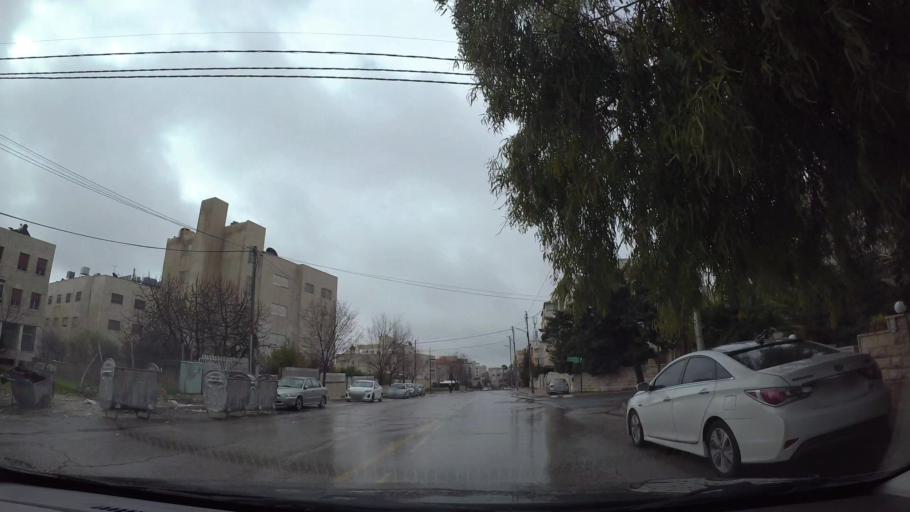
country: JO
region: Amman
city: Wadi as Sir
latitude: 31.9698
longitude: 35.8565
